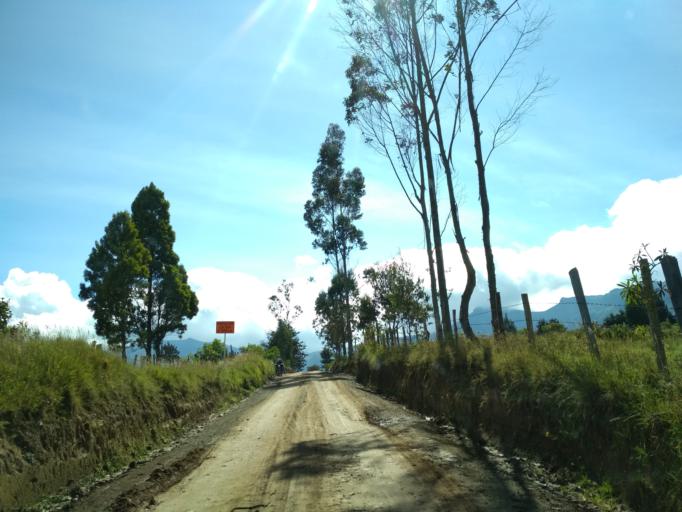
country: CO
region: Cauca
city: Silvia
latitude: 2.6932
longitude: -76.3342
